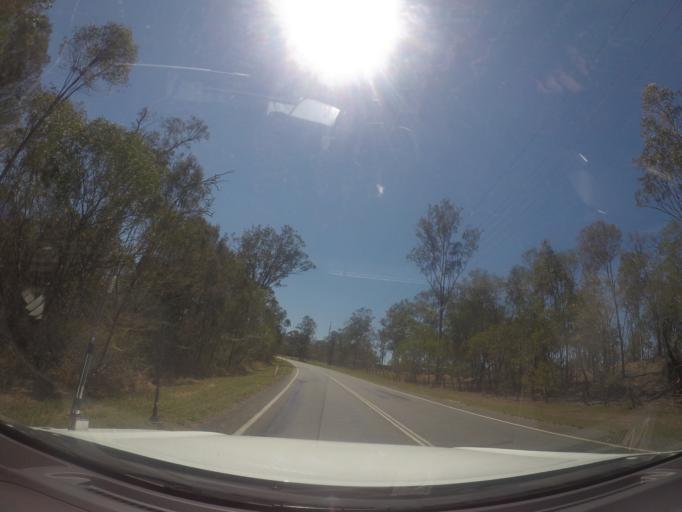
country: AU
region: Queensland
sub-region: Logan
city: North Maclean
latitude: -27.8098
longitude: 153.0421
